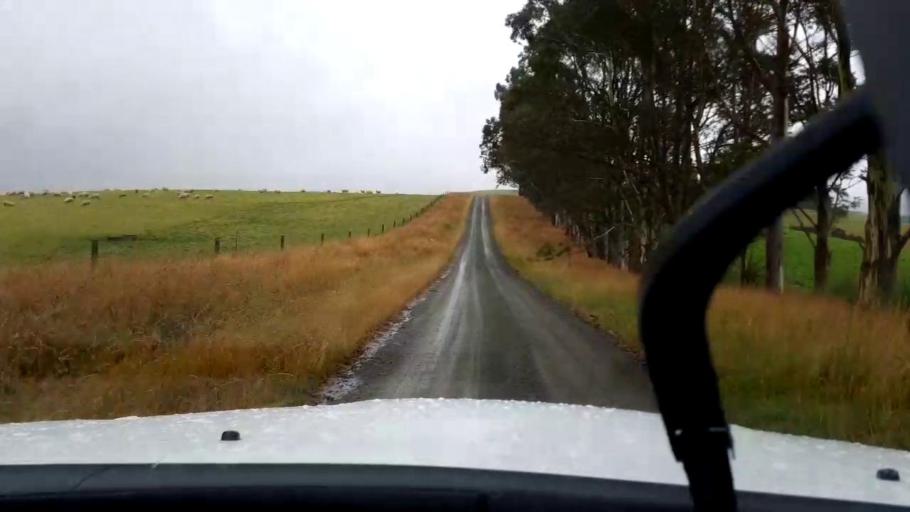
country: NZ
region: Canterbury
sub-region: Timaru District
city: Pleasant Point
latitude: -44.1723
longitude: 171.1037
